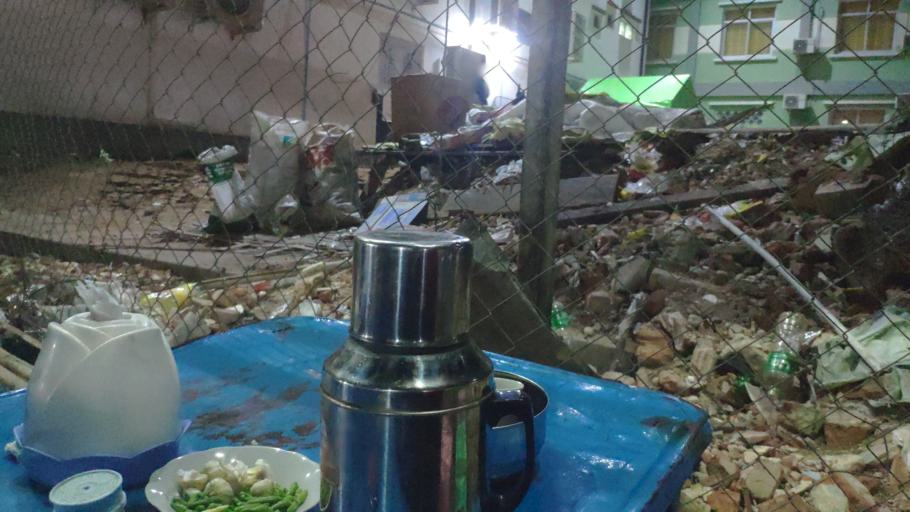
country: MM
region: Mandalay
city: Meiktila
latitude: 20.8777
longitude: 95.8589
